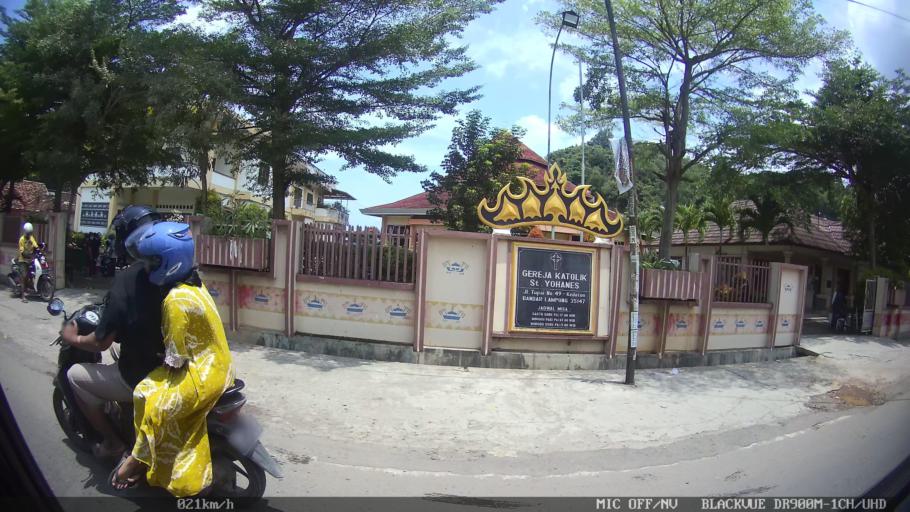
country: ID
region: Lampung
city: Kedaton
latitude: -5.3883
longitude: 105.2586
